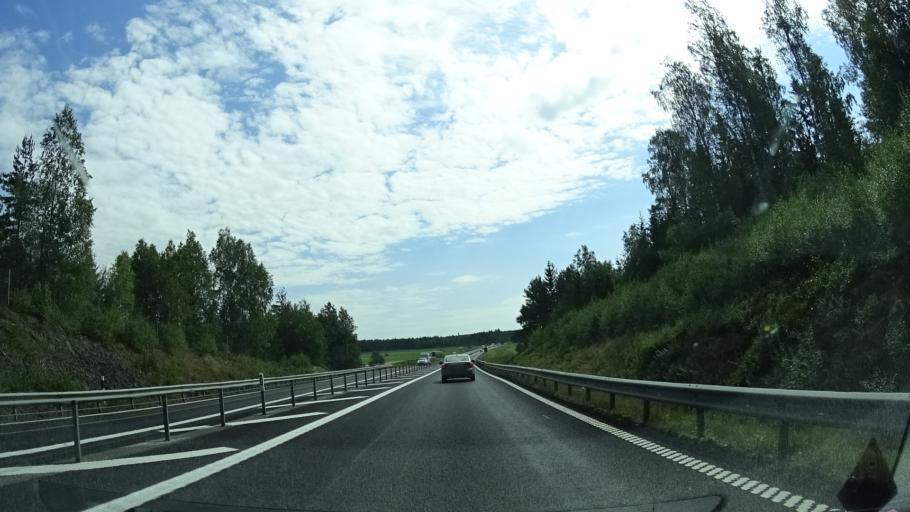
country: SE
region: Vaermland
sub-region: Karlstads Kommun
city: Skattkarr
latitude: 59.4164
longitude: 13.7378
